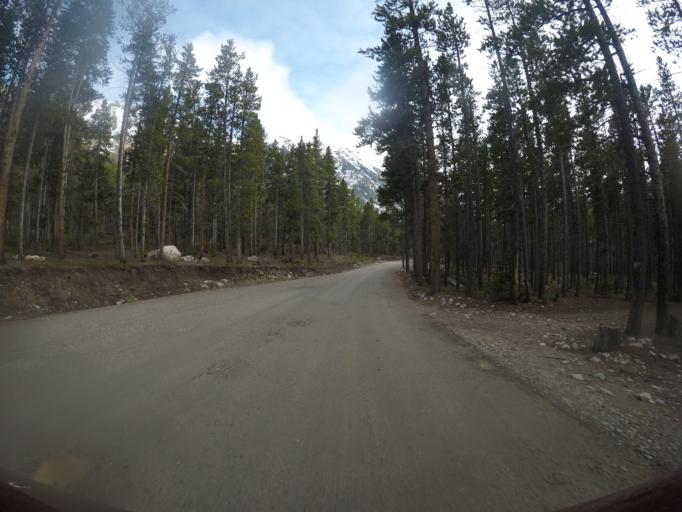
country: US
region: Montana
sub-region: Carbon County
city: Red Lodge
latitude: 45.0325
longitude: -109.4326
